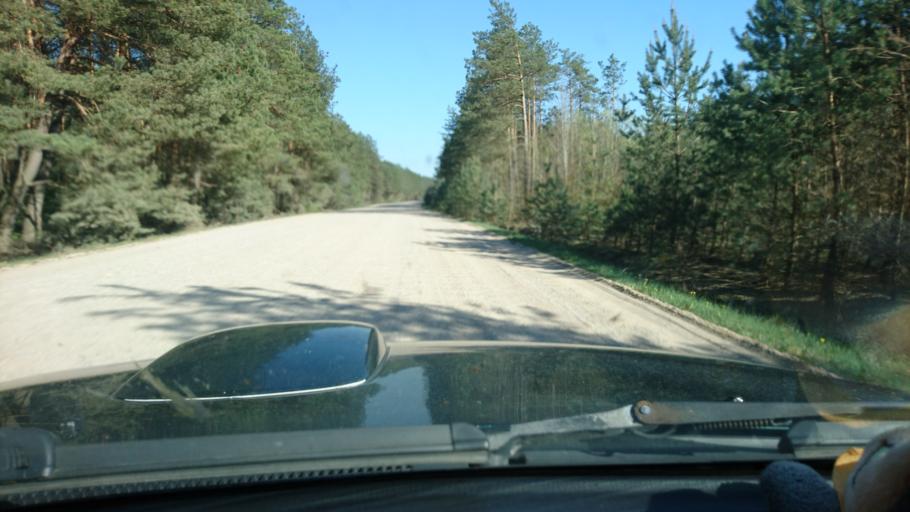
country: BY
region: Brest
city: Zhabinka
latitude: 52.3875
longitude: 24.1055
